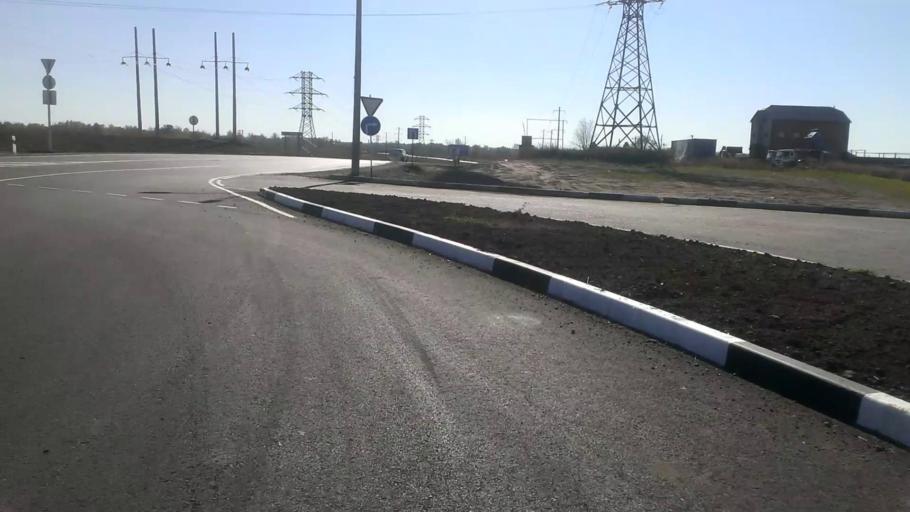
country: RU
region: Altai Krai
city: Sannikovo
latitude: 53.3366
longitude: 83.9384
